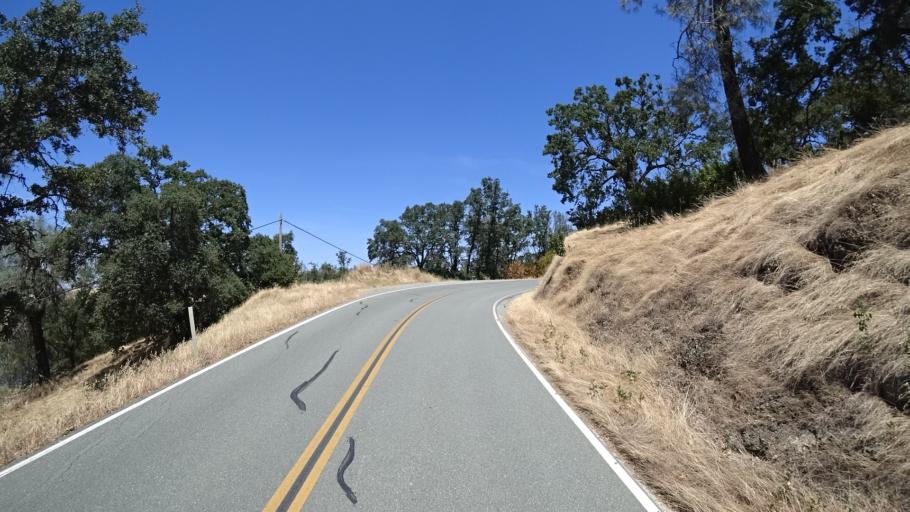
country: US
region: California
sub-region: Calaveras County
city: Valley Springs
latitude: 38.2401
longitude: -120.7875
